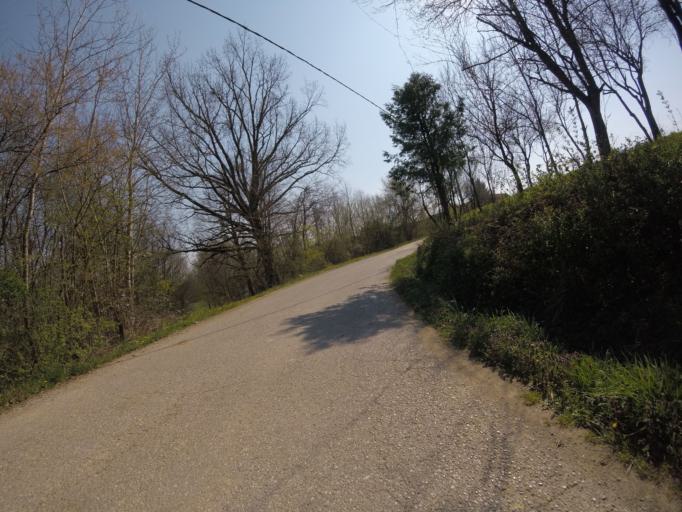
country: HR
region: Grad Zagreb
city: Strmec
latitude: 45.5890
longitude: 15.9239
